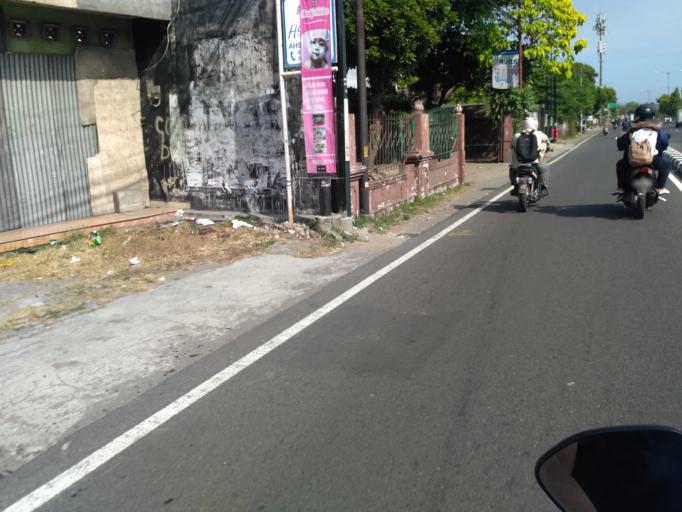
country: ID
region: Daerah Istimewa Yogyakarta
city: Depok
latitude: -7.7785
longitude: 110.4303
